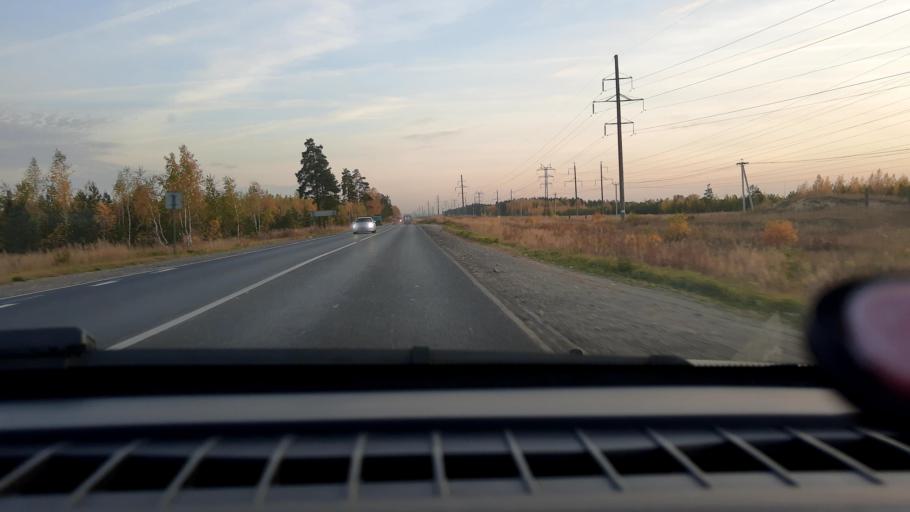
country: RU
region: Nizjnij Novgorod
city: Babino
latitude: 56.3213
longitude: 43.5590
